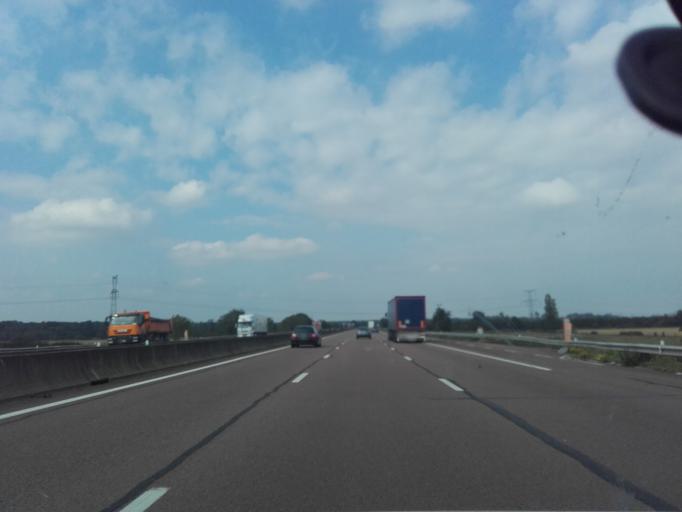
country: FR
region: Bourgogne
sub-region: Departement de Saone-et-Loire
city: Sennecey-le-Grand
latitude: 46.6629
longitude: 4.8534
